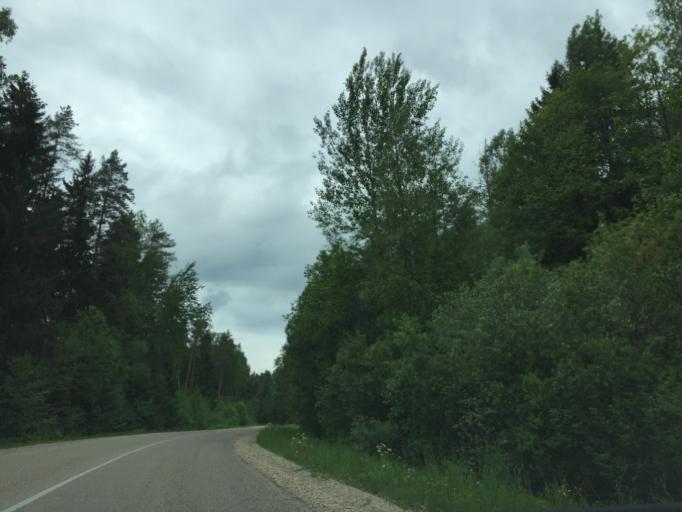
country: LV
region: Varkava
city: Vecvarkava
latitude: 56.0754
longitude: 26.6284
